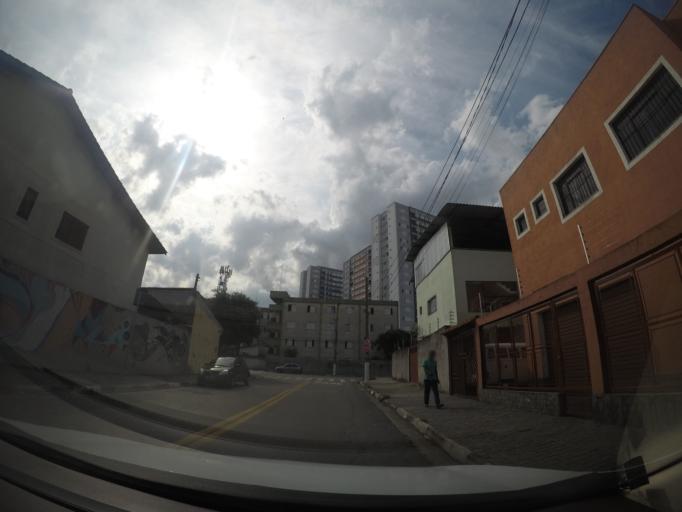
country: BR
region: Sao Paulo
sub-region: Guarulhos
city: Guarulhos
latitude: -23.4544
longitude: -46.5072
